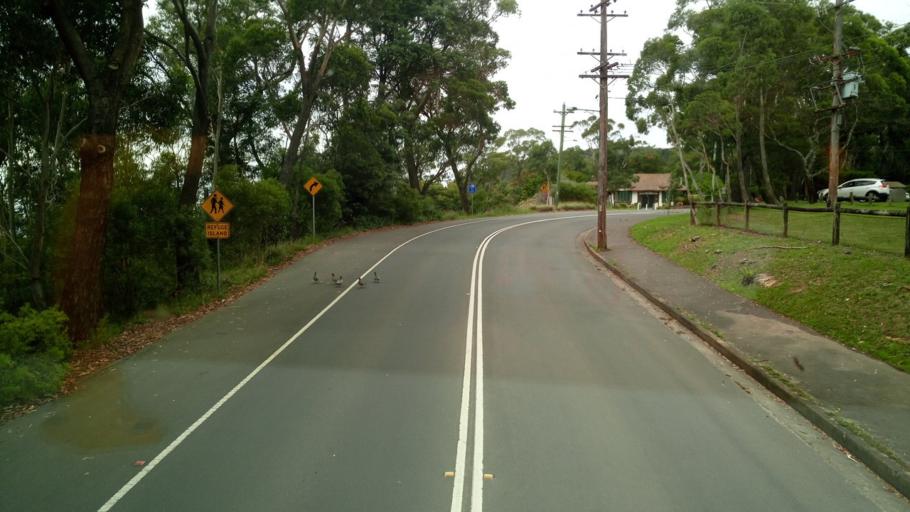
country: AU
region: New South Wales
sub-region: Blue Mountains Municipality
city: Katoomba
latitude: -33.7259
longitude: 150.3050
